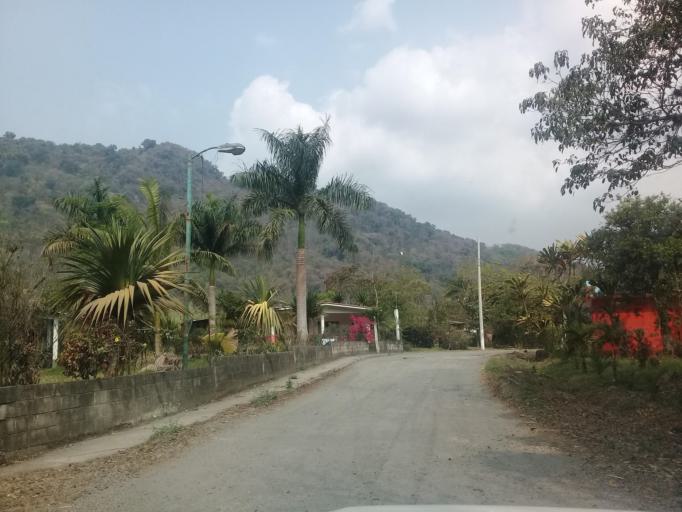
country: MX
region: Veracruz
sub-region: Ixtaczoquitlan
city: Capoluca
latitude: 18.8148
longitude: -96.9926
